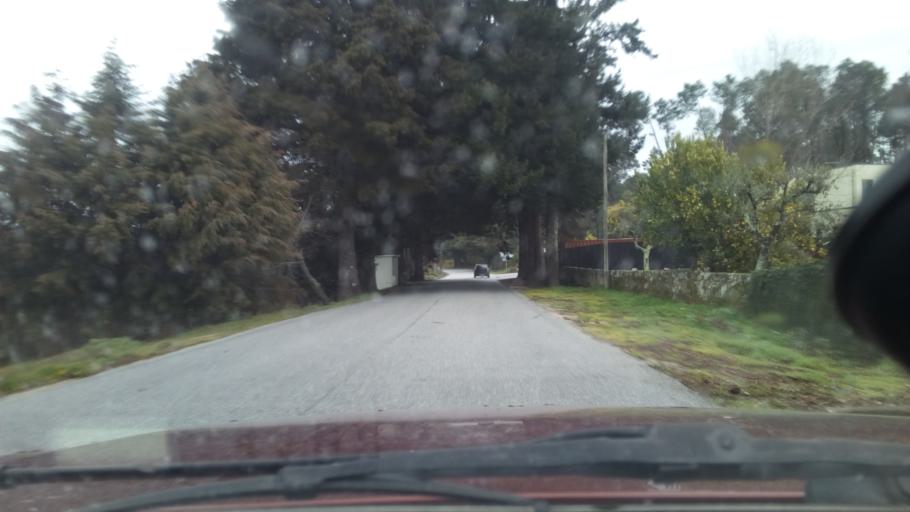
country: PT
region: Guarda
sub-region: Fornos de Algodres
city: Fornos de Algodres
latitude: 40.6086
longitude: -7.6291
